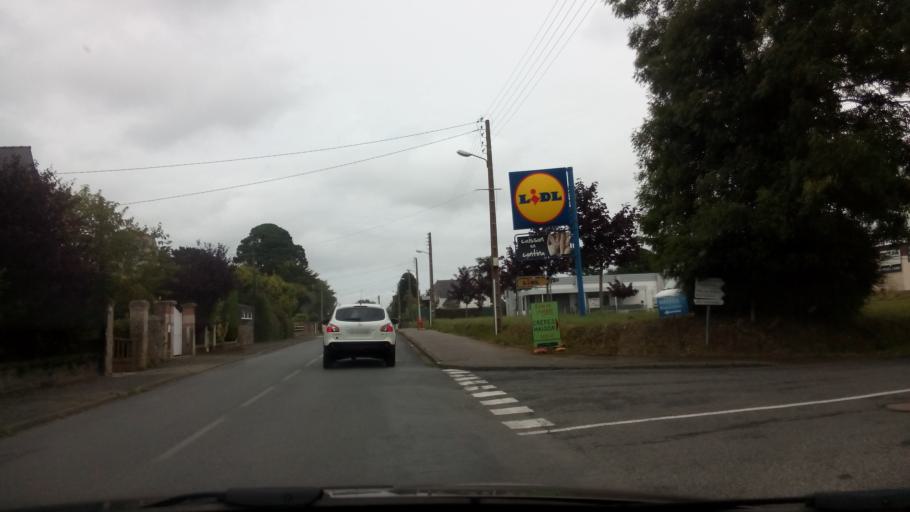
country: FR
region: Brittany
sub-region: Departement des Cotes-d'Armor
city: Plestin-les-Greves
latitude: 48.6627
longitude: -3.6275
